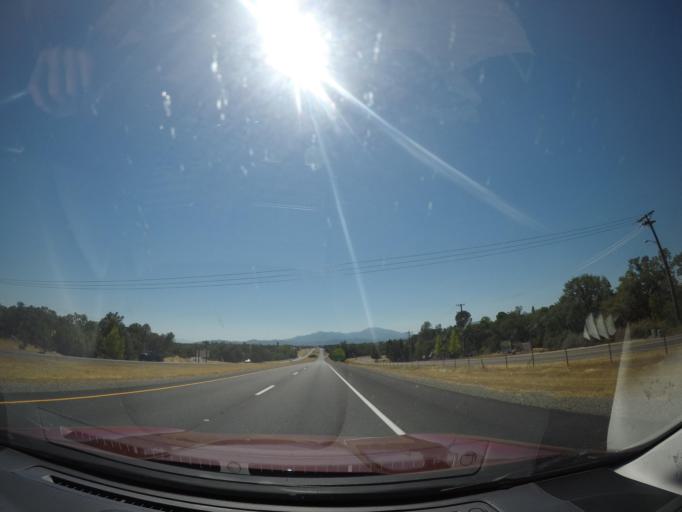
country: US
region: California
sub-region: Shasta County
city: Redding
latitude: 40.6165
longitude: -122.3407
